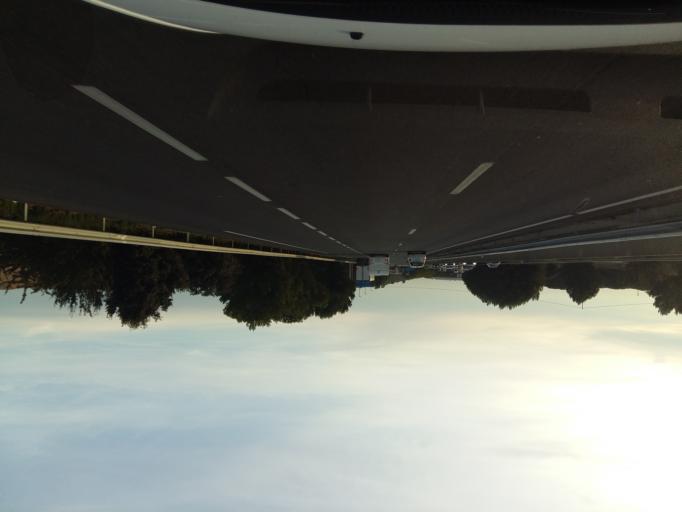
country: FR
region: Provence-Alpes-Cote d'Azur
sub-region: Departement des Bouches-du-Rhone
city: La Fare-les-Oliviers
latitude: 43.5880
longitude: 5.1988
